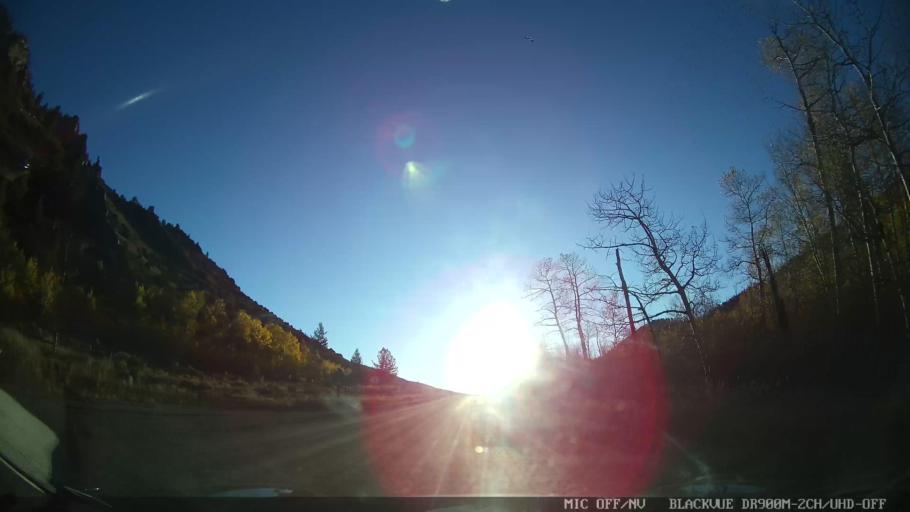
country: US
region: Colorado
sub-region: Grand County
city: Kremmling
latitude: 39.9939
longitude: -106.4708
